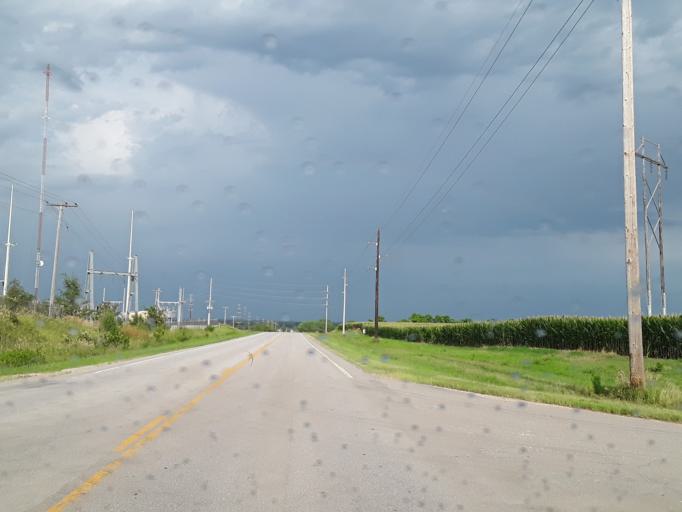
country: US
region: Nebraska
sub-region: Saunders County
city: Ashland
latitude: 41.0886
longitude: -96.3878
